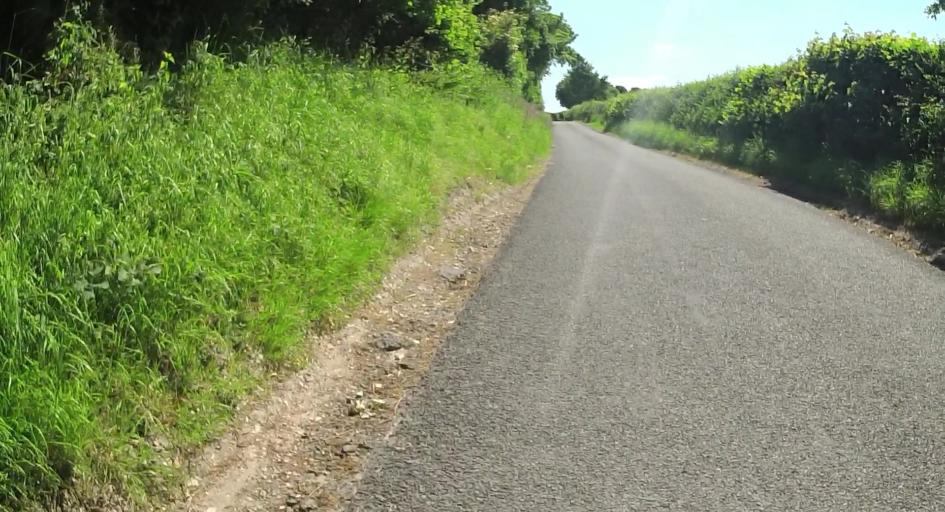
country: GB
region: England
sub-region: Hampshire
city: Kingsclere
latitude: 51.3257
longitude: -1.2924
